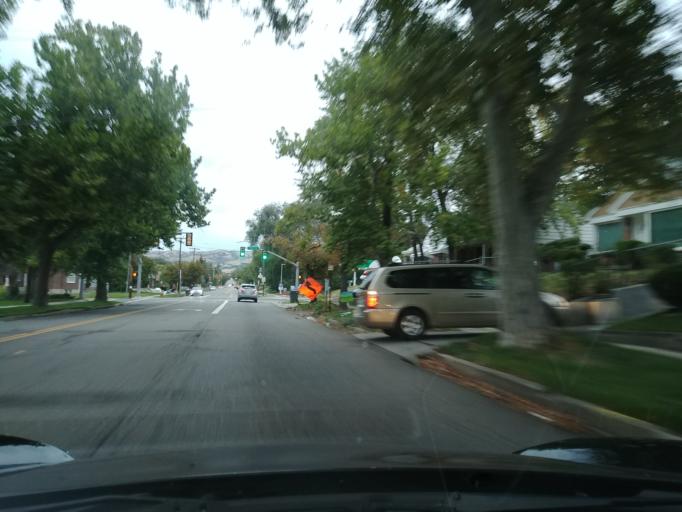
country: US
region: Utah
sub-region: Salt Lake County
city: Willard
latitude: 40.7329
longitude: -111.8539
